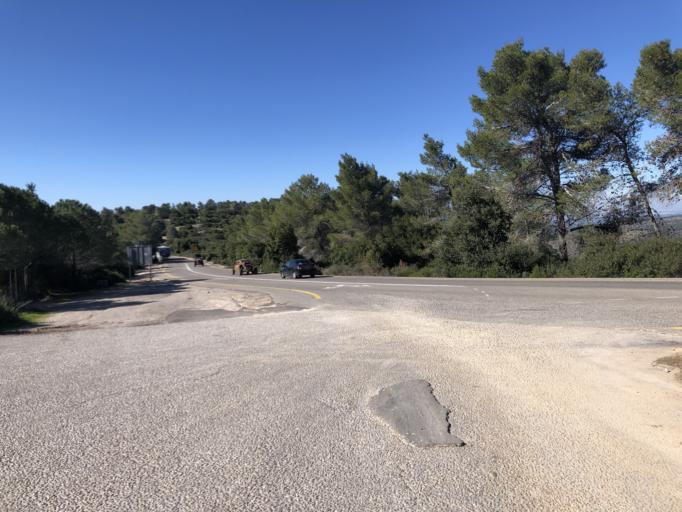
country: IL
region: Jerusalem
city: Zur Hadassa
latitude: 31.7478
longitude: 35.0492
